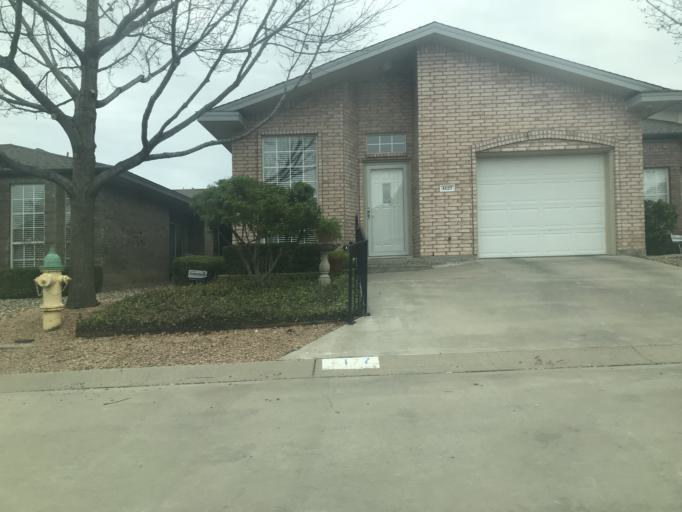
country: US
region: Texas
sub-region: Tom Green County
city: San Angelo
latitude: 31.4203
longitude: -100.4768
